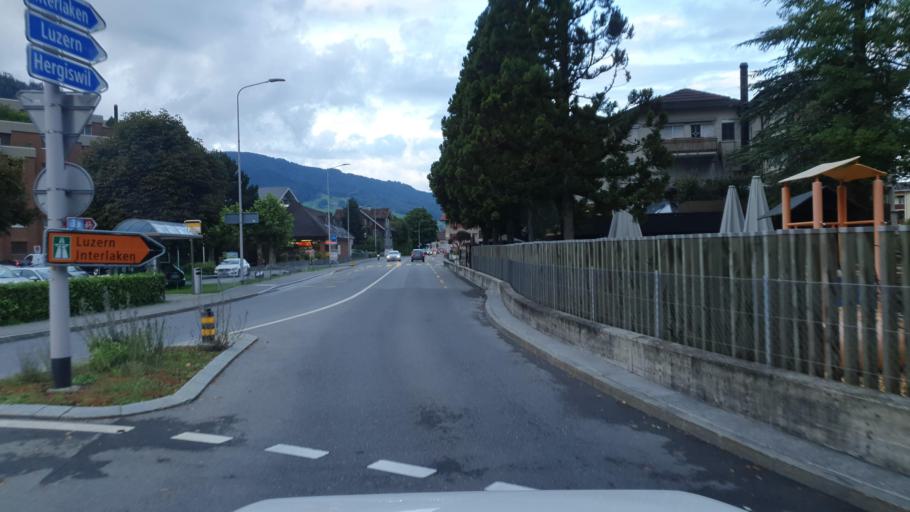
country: CH
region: Nidwalden
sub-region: Nidwalden
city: Stansstad
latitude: 46.9752
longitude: 8.3428
